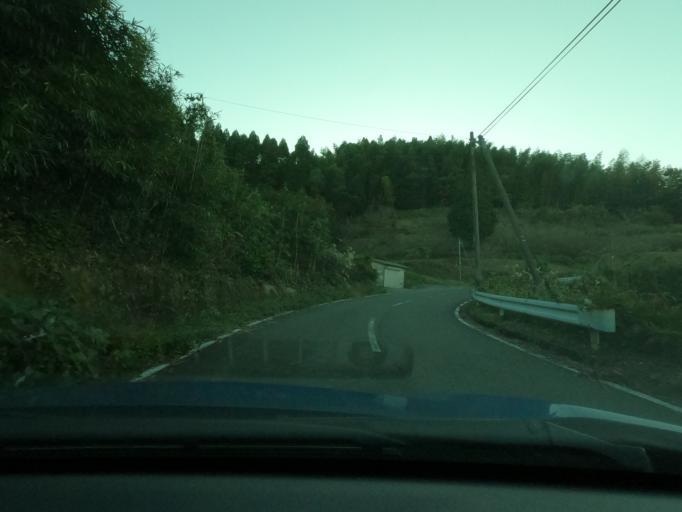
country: JP
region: Kagoshima
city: Satsumasendai
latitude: 31.8213
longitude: 130.4813
